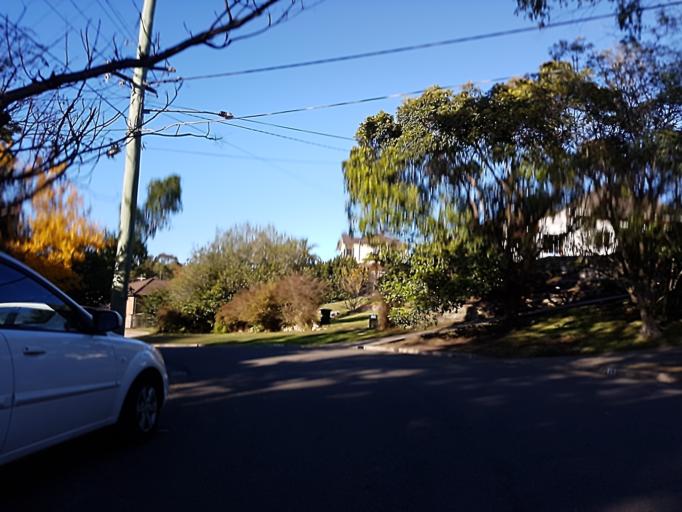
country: AU
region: New South Wales
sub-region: Manly Vale
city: Balgowlah
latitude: -33.7901
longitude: 151.2545
